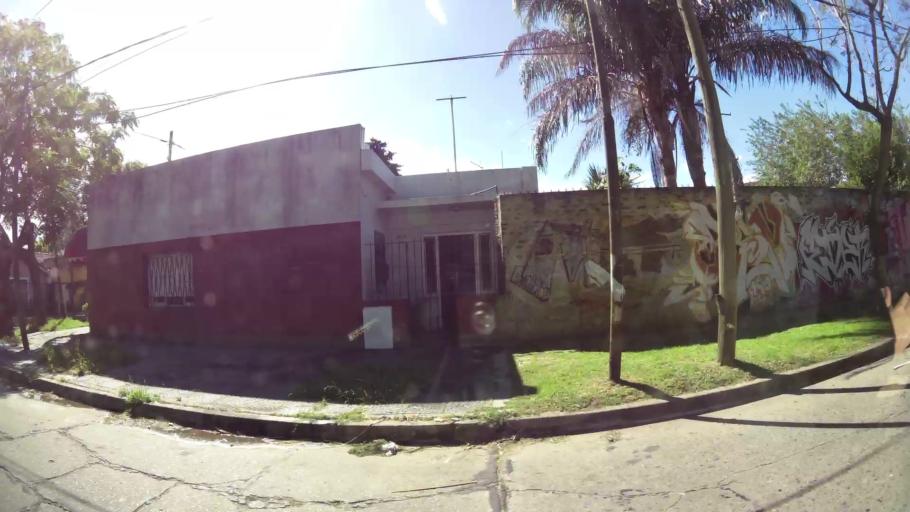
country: AR
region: Buenos Aires
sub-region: Partido de San Isidro
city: San Isidro
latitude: -34.5079
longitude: -58.5712
